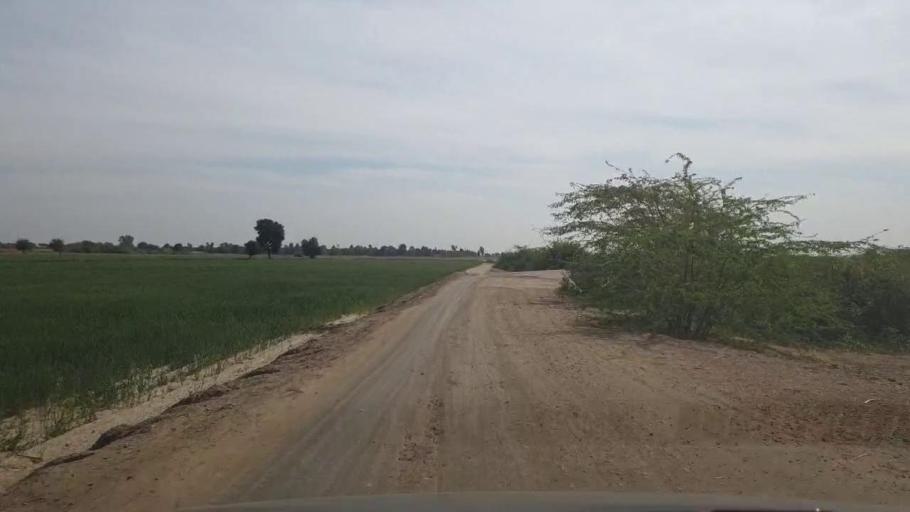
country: PK
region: Sindh
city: Kunri
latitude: 25.2802
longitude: 69.5969
